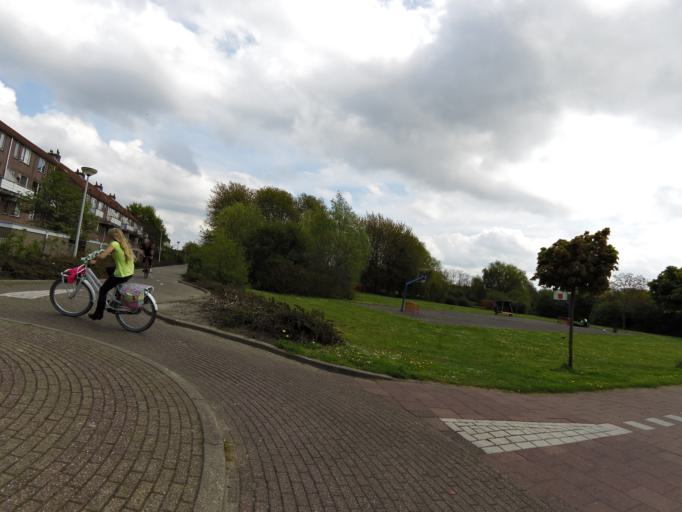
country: NL
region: South Holland
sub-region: Gemeente Hellevoetsluis
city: Hellevoetsluis
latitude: 51.8336
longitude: 4.1596
